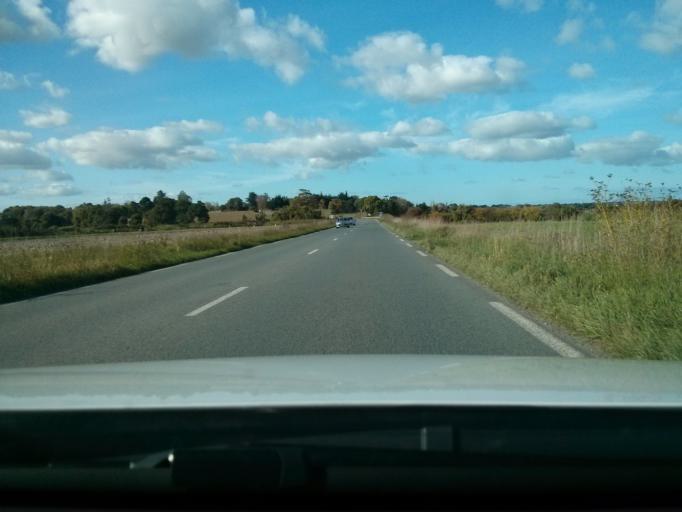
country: FR
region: Brittany
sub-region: Departement des Cotes-d'Armor
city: Ploubalay
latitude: 48.5767
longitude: -2.1634
